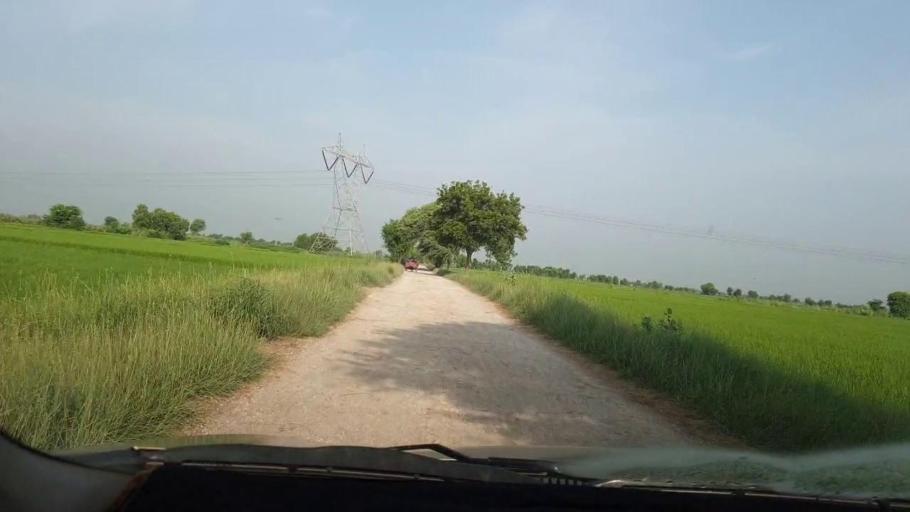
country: PK
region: Sindh
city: Goth Garelo
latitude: 27.4820
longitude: 68.0816
